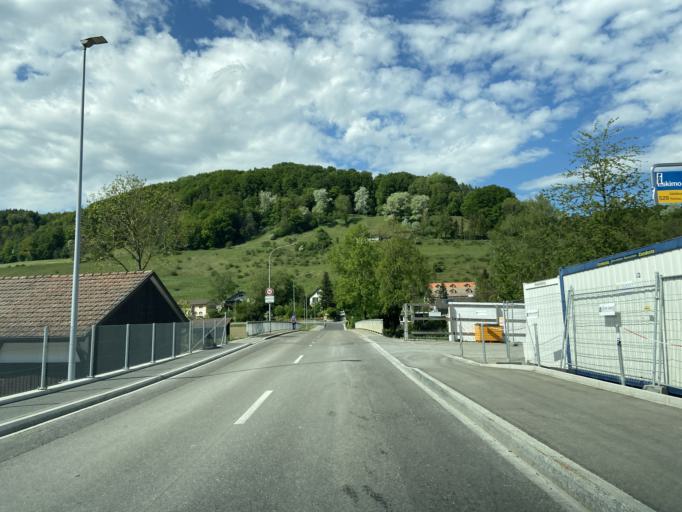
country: CH
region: Zurich
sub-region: Bezirk Winterthur
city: Pfungen
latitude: 47.5193
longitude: 8.6372
